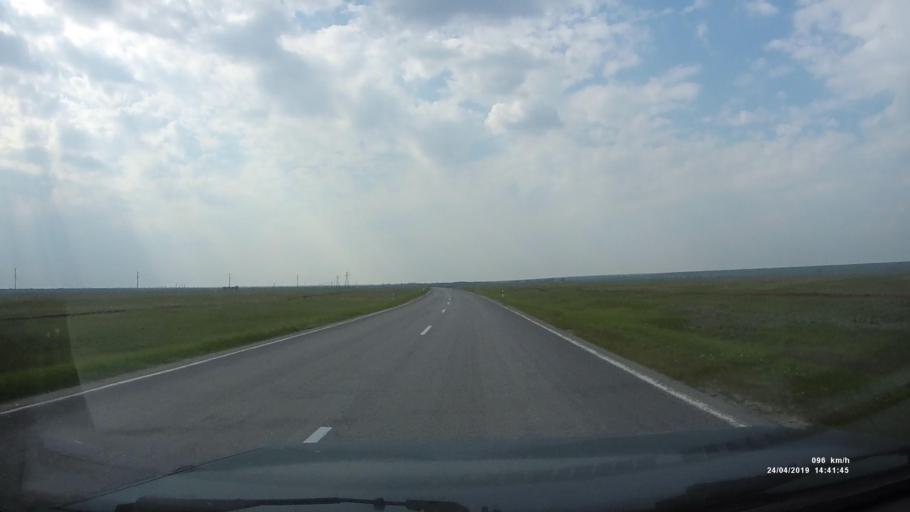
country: RU
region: Rostov
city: Remontnoye
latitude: 46.4477
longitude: 43.8749
